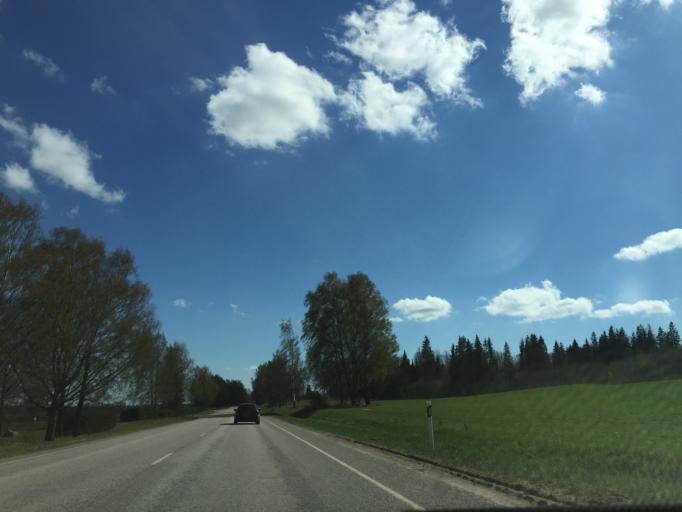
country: EE
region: Valgamaa
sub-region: Valga linn
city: Valga
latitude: 57.8911
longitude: 26.0555
